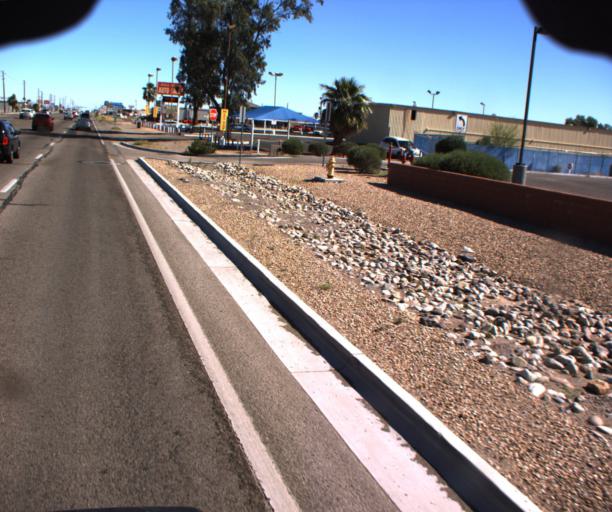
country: US
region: Arizona
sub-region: Mohave County
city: Mohave Valley
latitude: 35.0191
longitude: -114.5979
